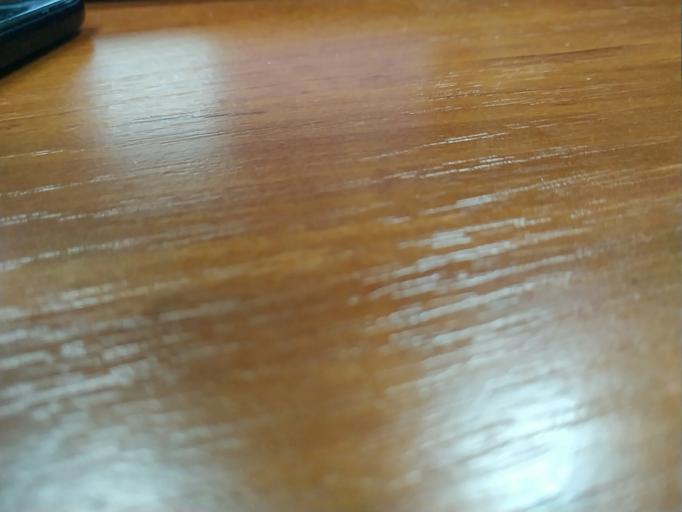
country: RU
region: Moskovskaya
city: Domodedovo
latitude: 55.3689
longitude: 37.6884
